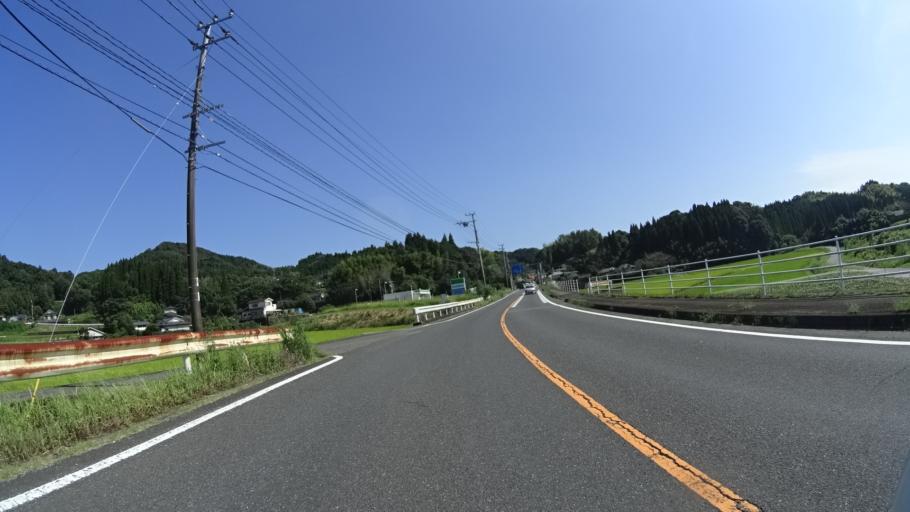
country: JP
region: Kagoshima
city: Kajiki
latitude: 31.7575
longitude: 130.6761
